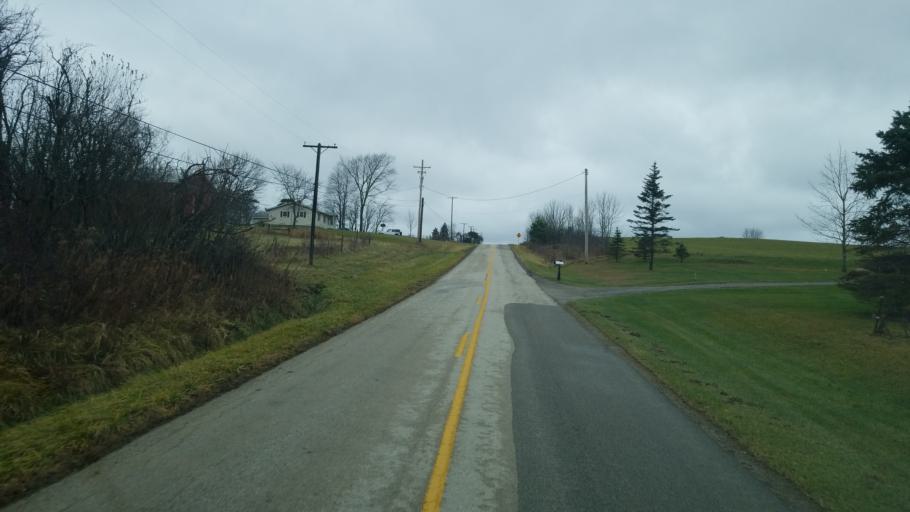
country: US
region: Ohio
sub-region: Ashtabula County
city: North Kingsville
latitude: 41.8600
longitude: -80.6175
